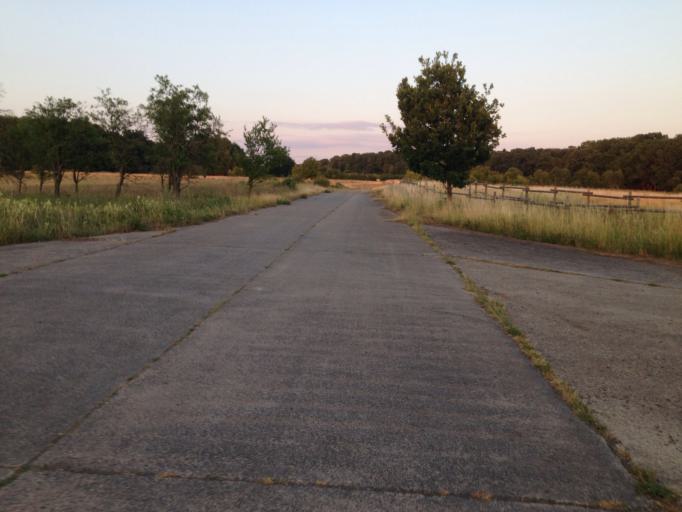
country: DE
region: Hesse
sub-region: Regierungsbezirk Giessen
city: Grossen Buseck
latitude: 50.5679
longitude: 8.7461
